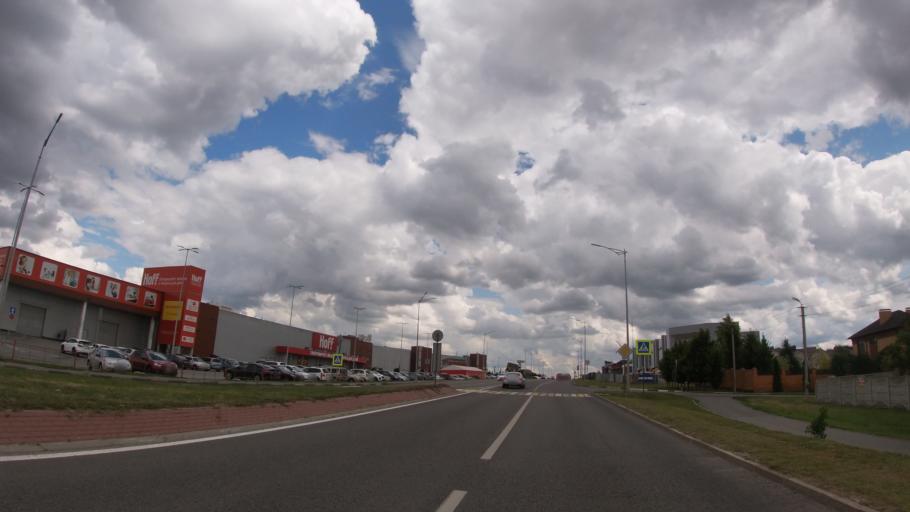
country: RU
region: Belgorod
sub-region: Belgorodskiy Rayon
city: Belgorod
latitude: 50.5510
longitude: 36.5637
